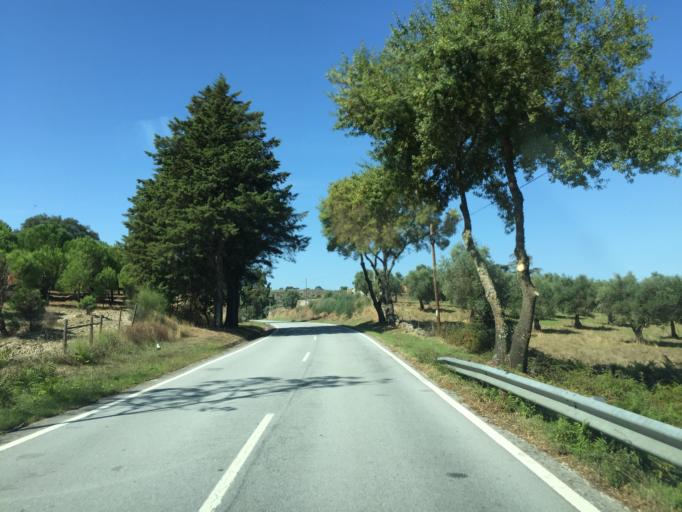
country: PT
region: Portalegre
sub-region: Portalegre
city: Alagoa
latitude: 39.4341
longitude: -7.5325
